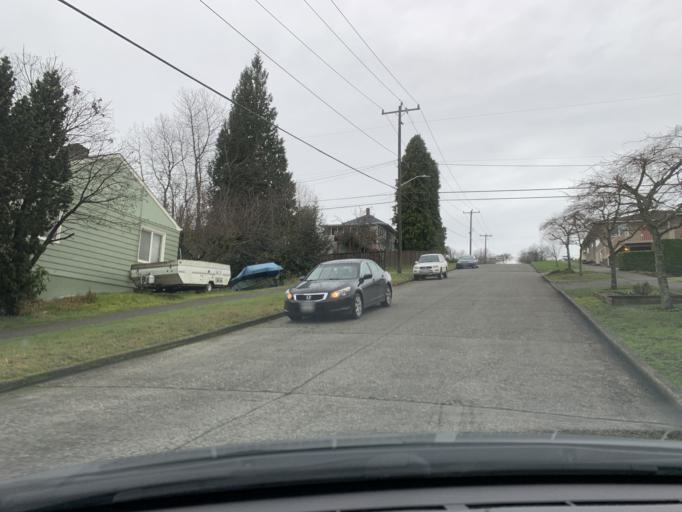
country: US
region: Washington
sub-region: King County
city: White Center
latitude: 47.5557
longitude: -122.3830
